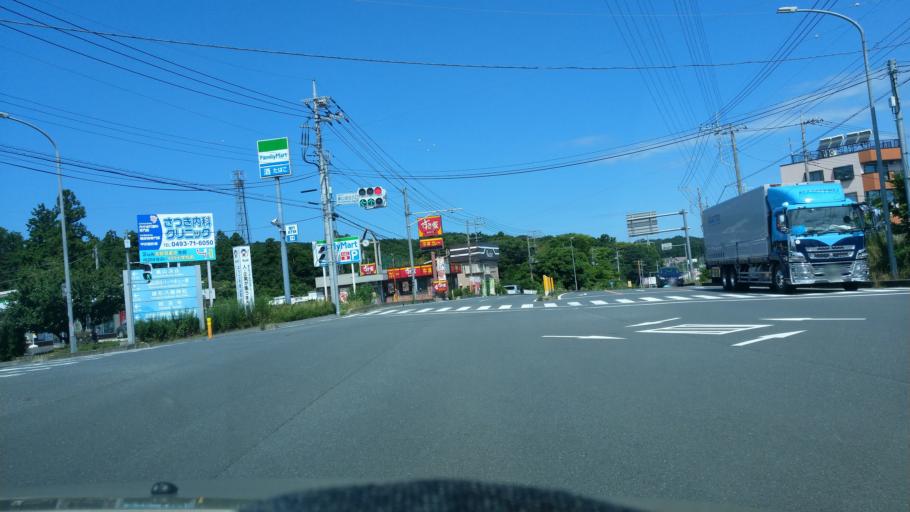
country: JP
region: Saitama
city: Ogawa
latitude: 36.0394
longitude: 139.3183
